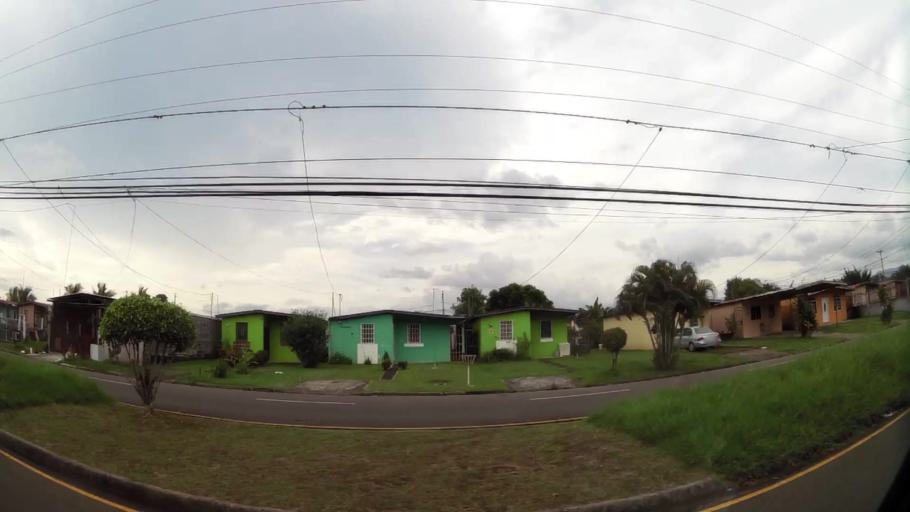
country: PA
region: Panama
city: Cabra Numero Uno
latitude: 9.0923
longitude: -79.3418
